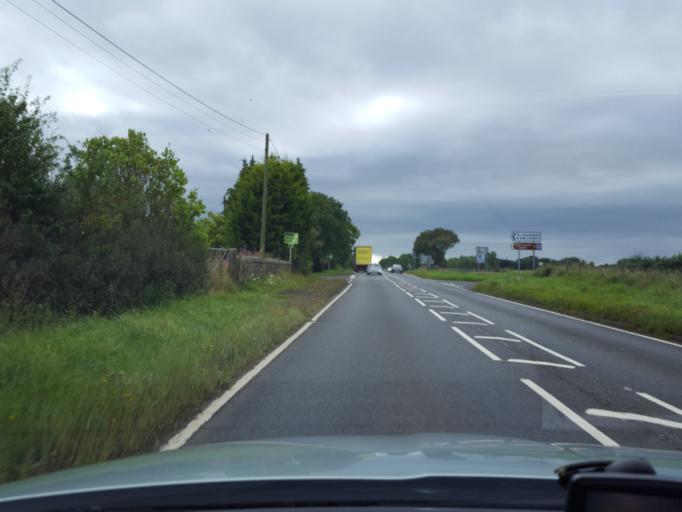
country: GB
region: Scotland
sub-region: Perth and Kinross
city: Milnathort
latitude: 56.2451
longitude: -3.3744
